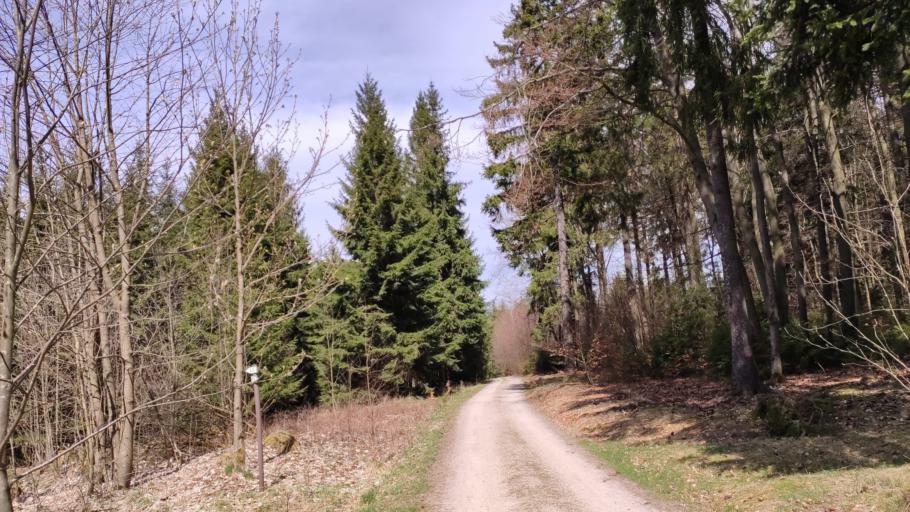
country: DE
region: Bavaria
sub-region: Upper Franconia
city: Reichenbach
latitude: 50.4649
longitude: 11.4539
